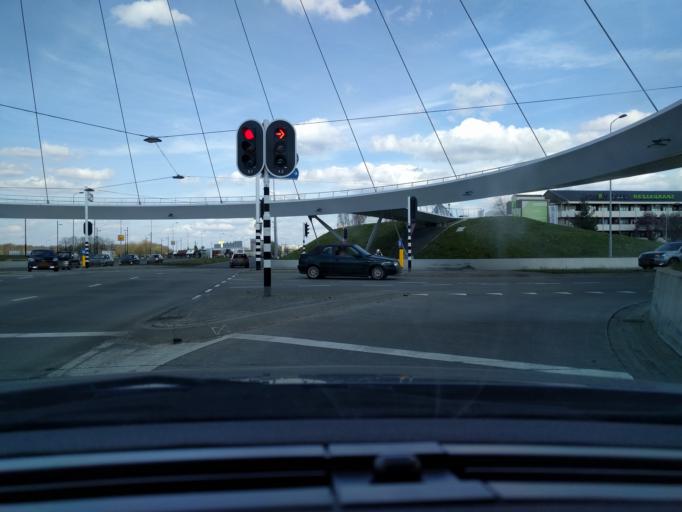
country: NL
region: North Brabant
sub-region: Gemeente Eindhoven
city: Meerhoven
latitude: 51.4332
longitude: 5.4194
